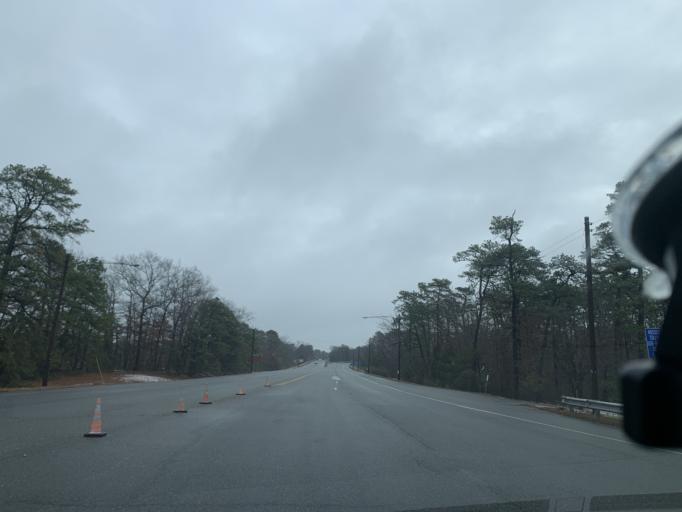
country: US
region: New Jersey
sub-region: Atlantic County
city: Pomona
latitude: 39.4497
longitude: -74.6304
